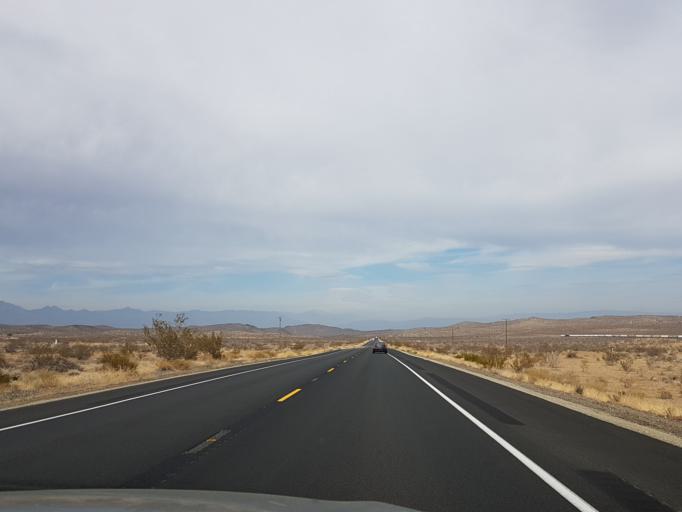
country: US
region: California
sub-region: Kern County
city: Ridgecrest
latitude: 35.5012
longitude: -117.6645
